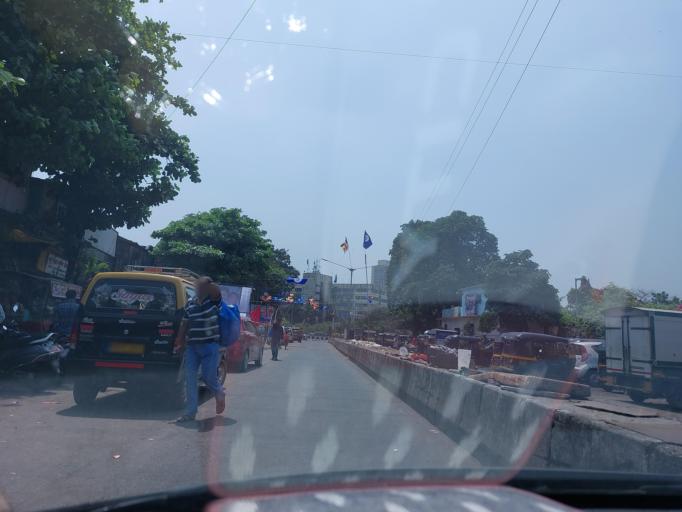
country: IN
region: Maharashtra
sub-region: Mumbai Suburban
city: Mumbai
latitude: 19.0557
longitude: 72.8843
